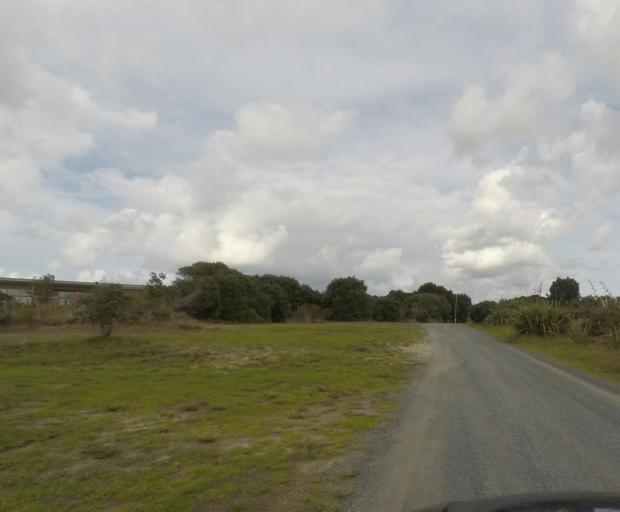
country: NZ
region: Northland
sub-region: Whangarei
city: Ruakaka
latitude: -35.9345
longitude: 174.4574
